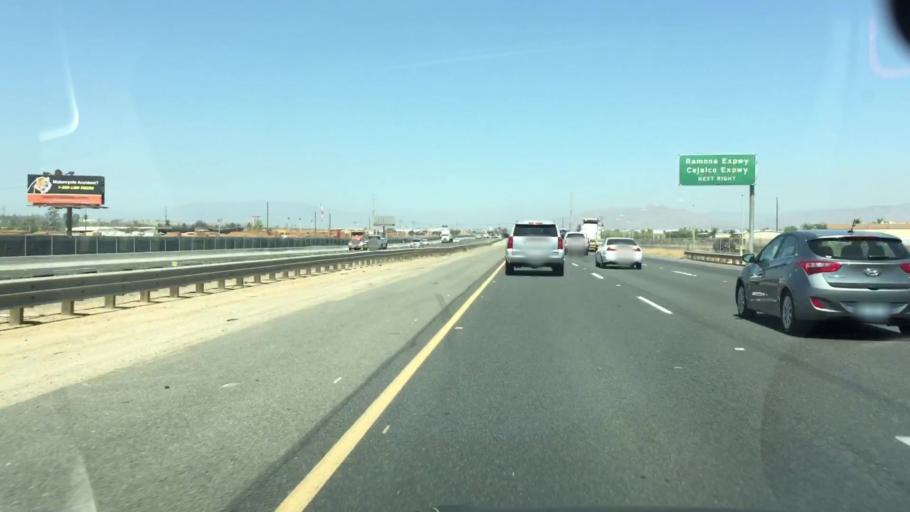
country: US
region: California
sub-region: Riverside County
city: Mead Valley
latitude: 33.8341
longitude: -117.2467
